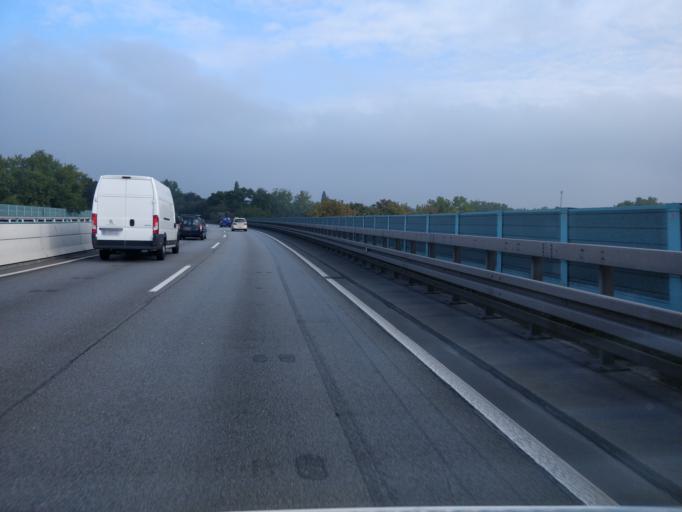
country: DE
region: North Rhine-Westphalia
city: Meiderich
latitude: 51.5015
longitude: 6.7643
